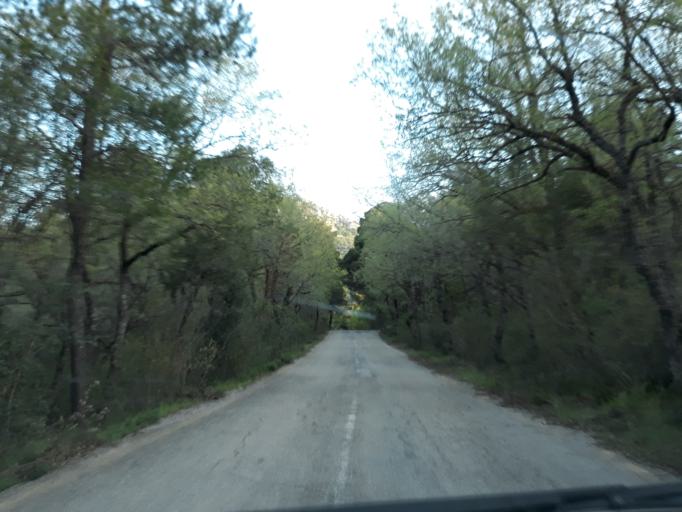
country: GR
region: Attica
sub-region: Nomarchia Anatolikis Attikis
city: Afidnes
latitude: 38.1959
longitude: 23.7838
